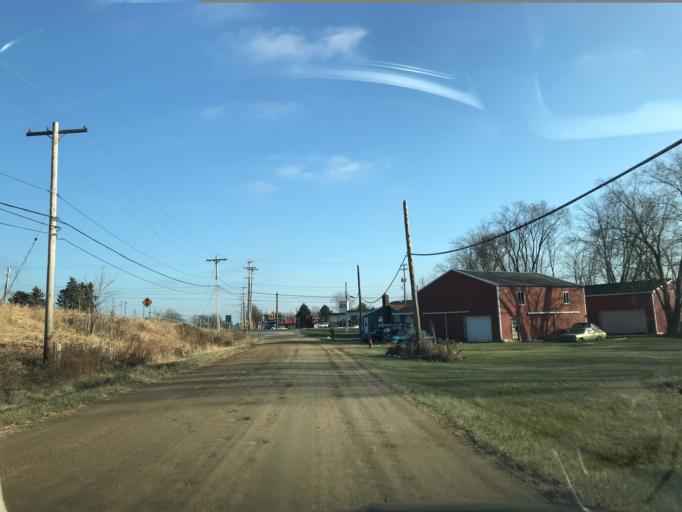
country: US
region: Michigan
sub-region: Ingham County
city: Edgemont Park
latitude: 42.7704
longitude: -84.6040
